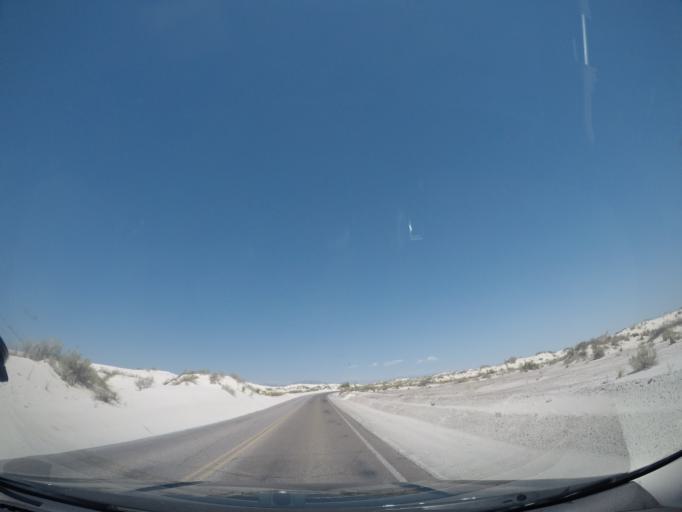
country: US
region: New Mexico
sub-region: Otero County
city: Holloman Air Force Base
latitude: 32.7939
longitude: -106.2409
